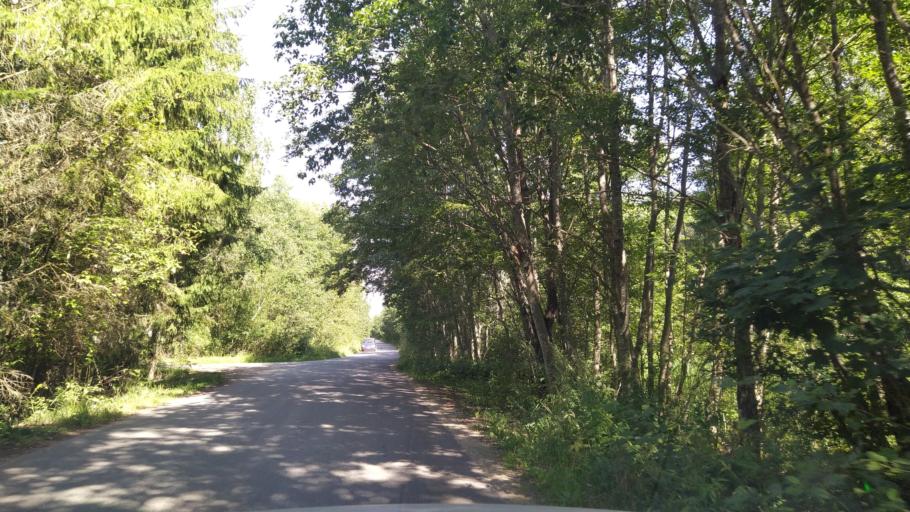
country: RU
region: Leningrad
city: Rozhdestveno
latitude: 59.2774
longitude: 30.0276
